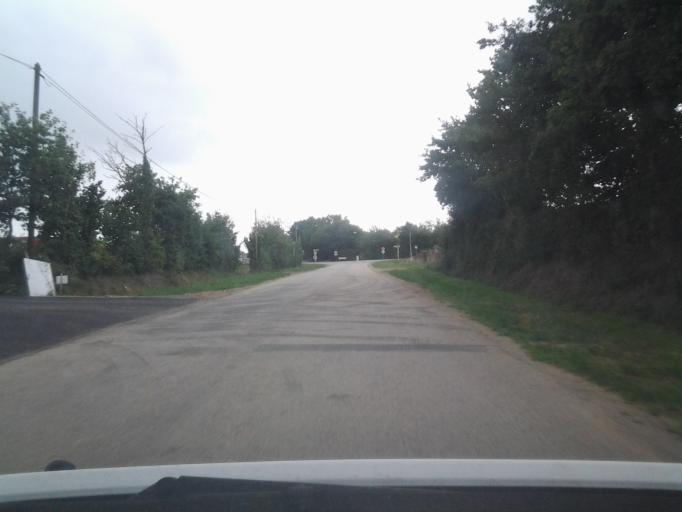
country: FR
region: Pays de la Loire
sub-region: Departement de la Vendee
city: La Roche-sur-Yon
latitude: 46.6898
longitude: -1.4223
